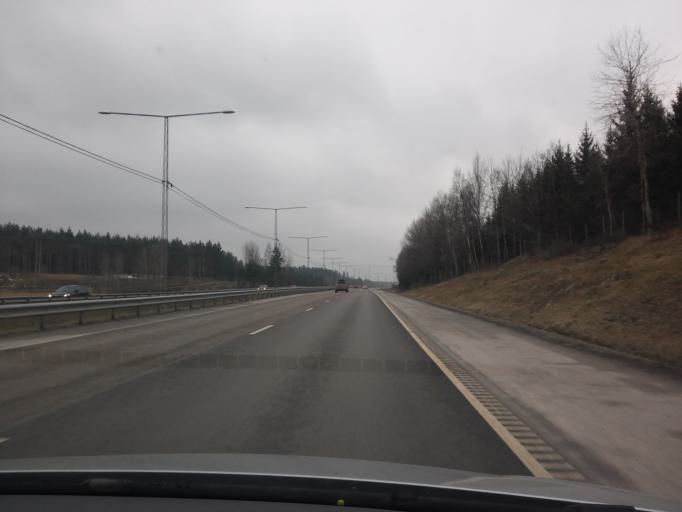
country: SE
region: Stockholm
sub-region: Vallentuna Kommun
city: Vallentuna
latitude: 59.4806
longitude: 18.1642
